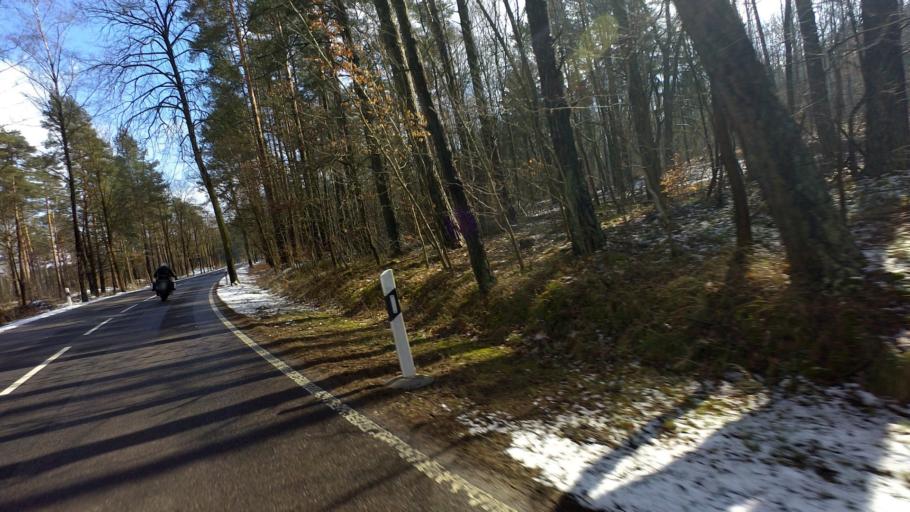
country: DE
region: Brandenburg
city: Rudnitz
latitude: 52.7017
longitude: 13.6363
